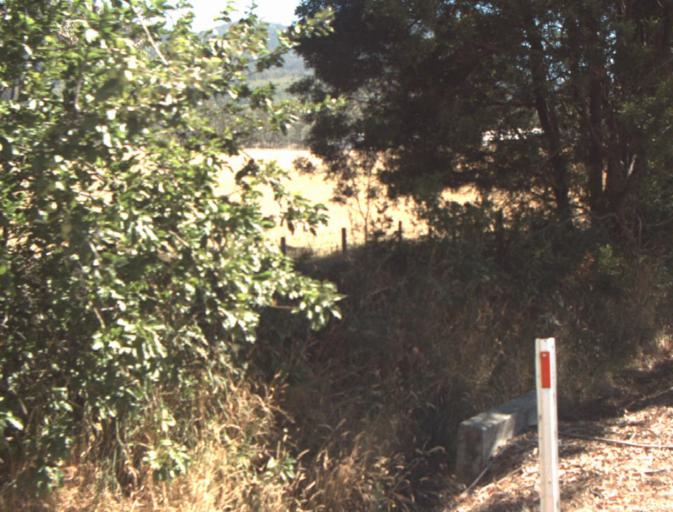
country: AU
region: Tasmania
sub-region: Launceston
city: Newstead
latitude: -41.3380
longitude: 147.3039
